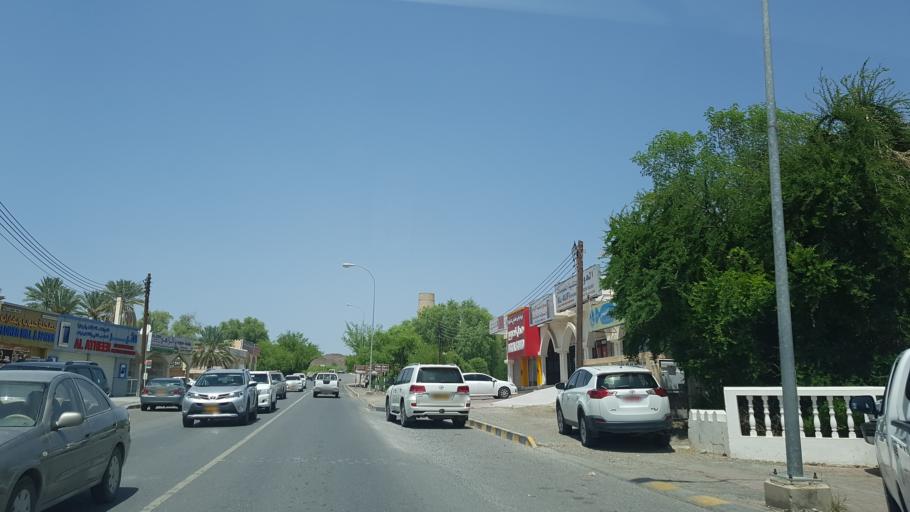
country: OM
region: Muhafazat ad Dakhiliyah
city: Bahla'
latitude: 22.9628
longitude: 57.2989
